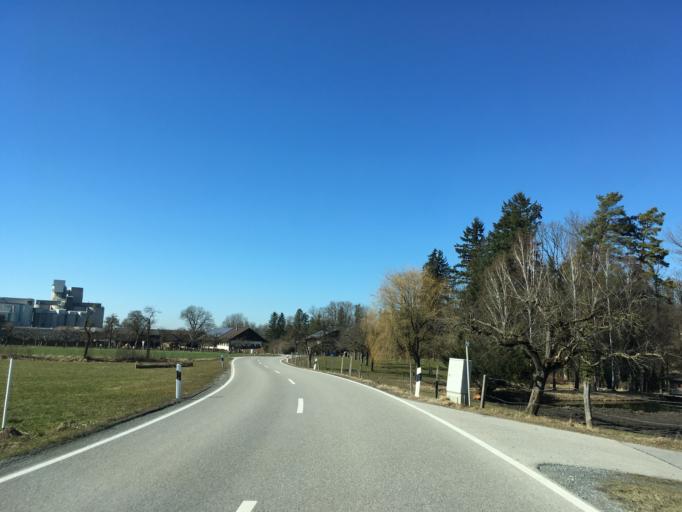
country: DE
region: Bavaria
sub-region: Upper Bavaria
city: Samerberg
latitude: 47.7927
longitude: 12.1905
